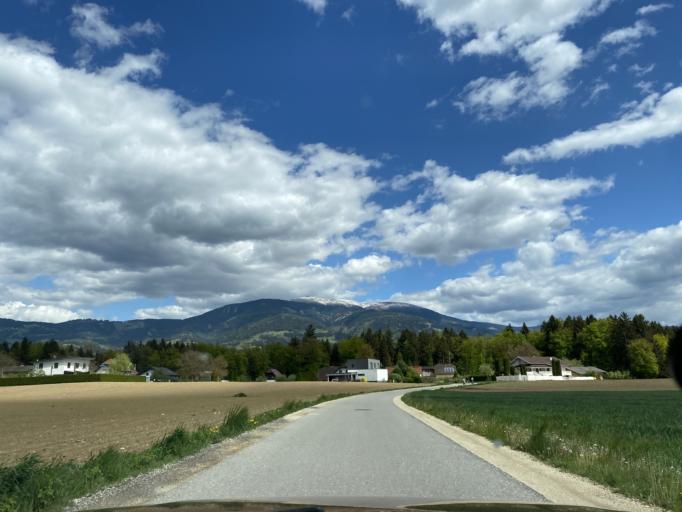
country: AT
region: Carinthia
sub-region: Politischer Bezirk Wolfsberg
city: Sankt Andrae
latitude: 46.7864
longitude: 14.8285
